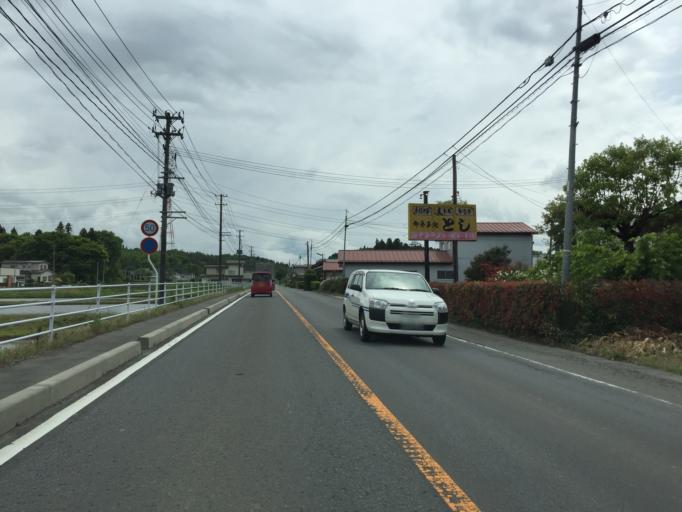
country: JP
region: Fukushima
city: Ishikawa
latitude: 37.0597
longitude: 140.3742
